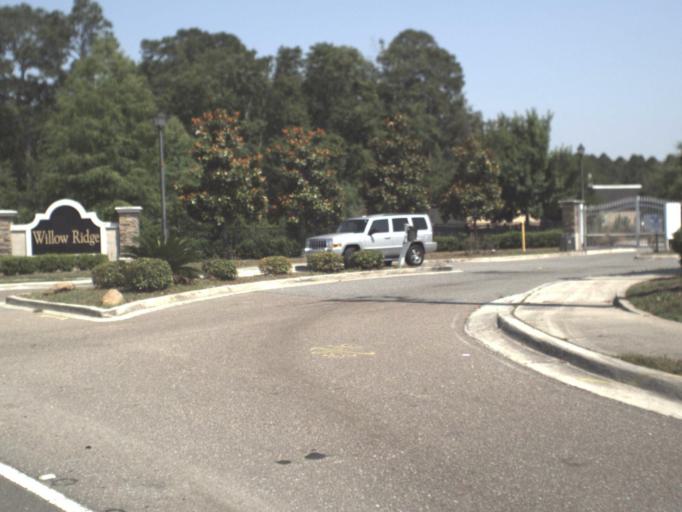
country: US
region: Florida
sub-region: Clay County
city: Bellair-Meadowbrook Terrace
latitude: 30.2697
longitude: -81.7698
